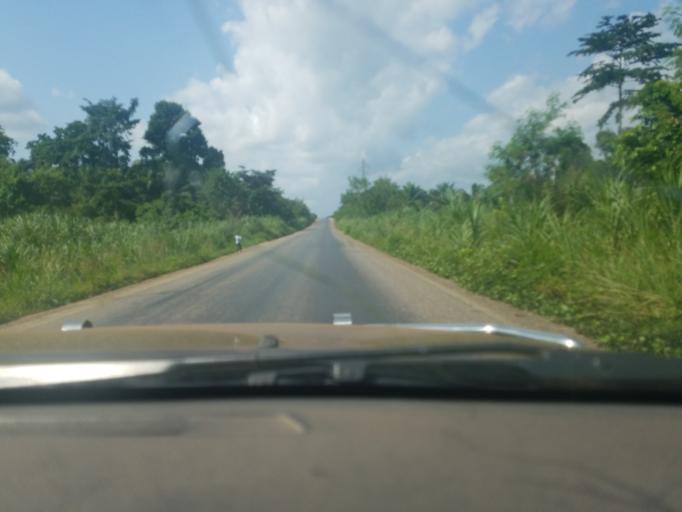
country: GH
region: Western
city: Bibiani
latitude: 6.8810
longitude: -2.4230
